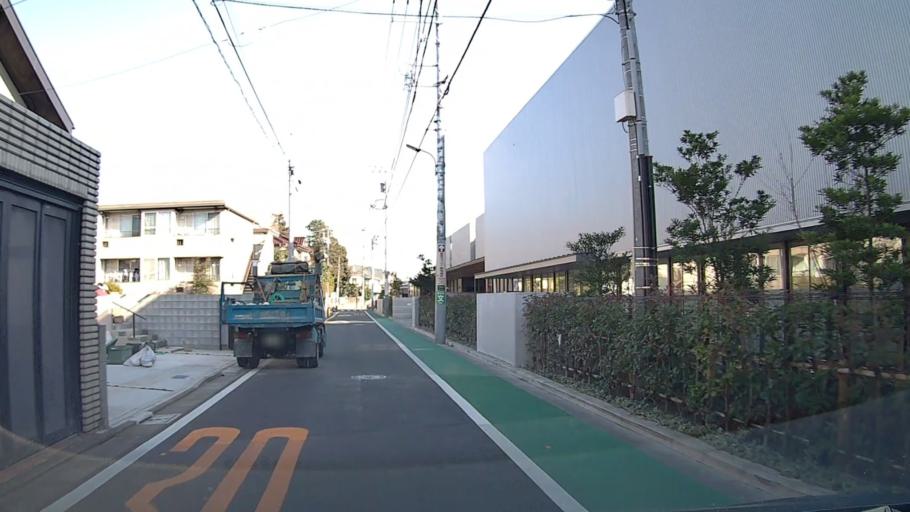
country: JP
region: Tokyo
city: Musashino
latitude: 35.7313
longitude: 139.6049
